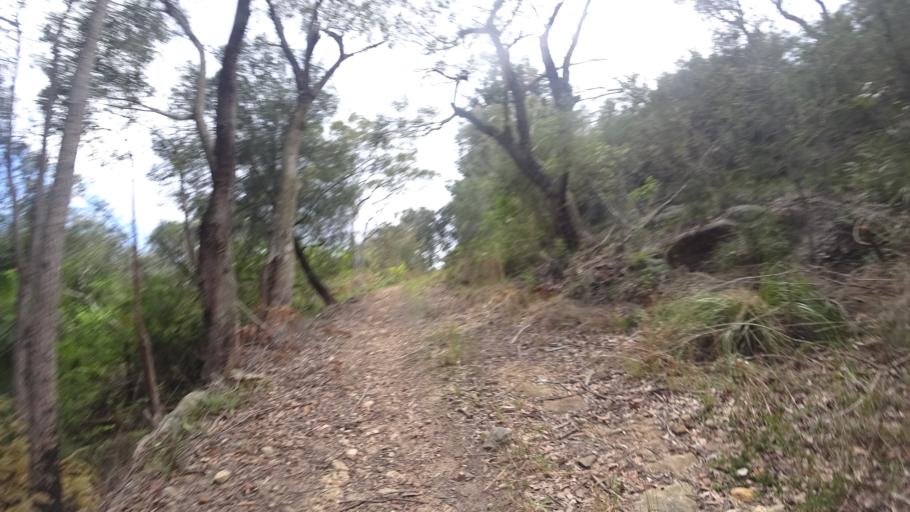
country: AU
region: New South Wales
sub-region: City of Sydney
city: North Turramurra
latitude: -33.6816
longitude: 151.1936
